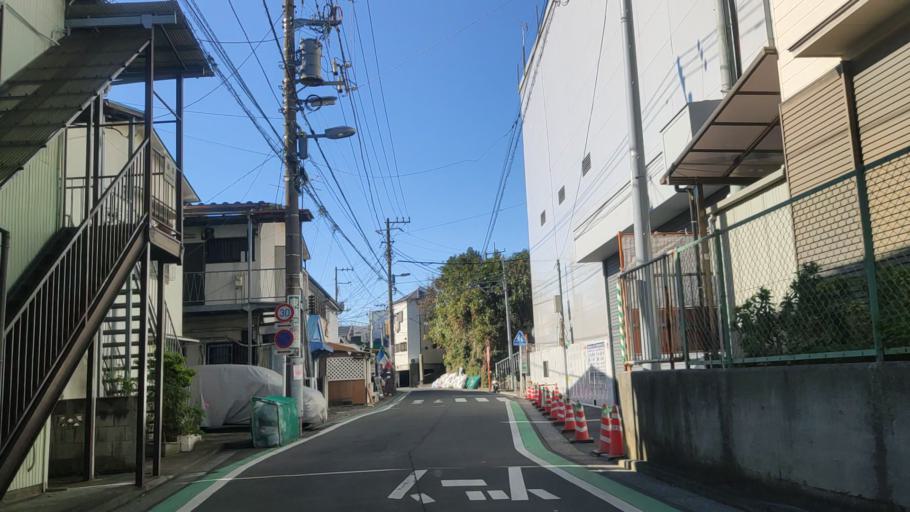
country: JP
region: Kanagawa
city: Yokohama
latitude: 35.4250
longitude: 139.6460
